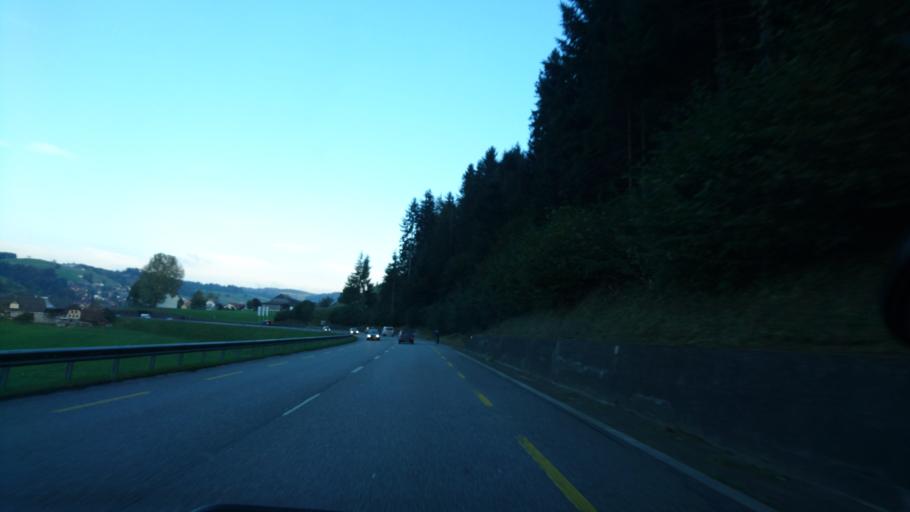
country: CH
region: Bern
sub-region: Emmental District
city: Langnau
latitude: 46.9391
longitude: 7.7681
